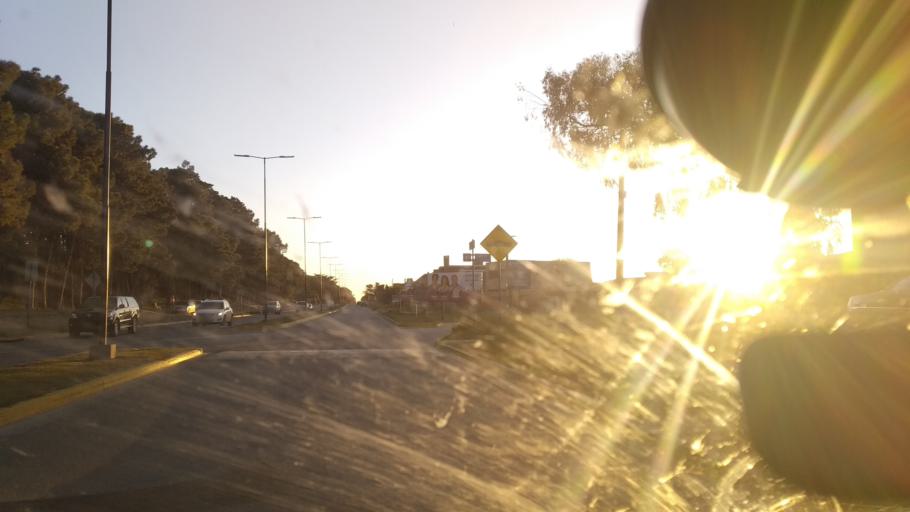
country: AR
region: Buenos Aires
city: Necochea
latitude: -38.5826
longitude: -58.7431
